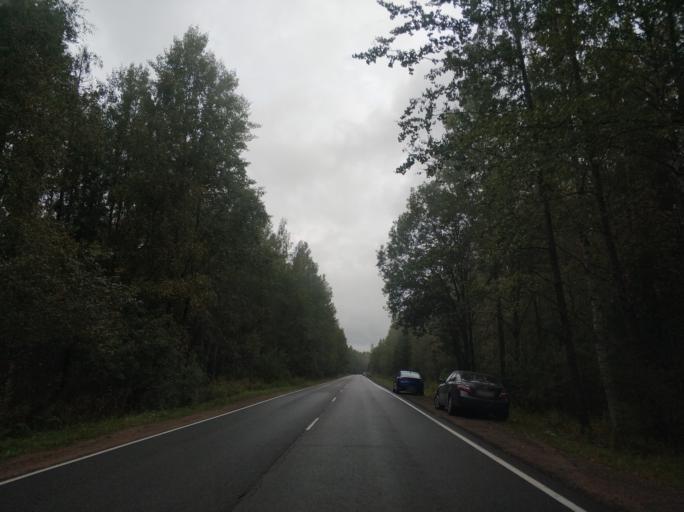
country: RU
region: Leningrad
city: Borisova Griva
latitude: 60.1568
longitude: 30.9285
